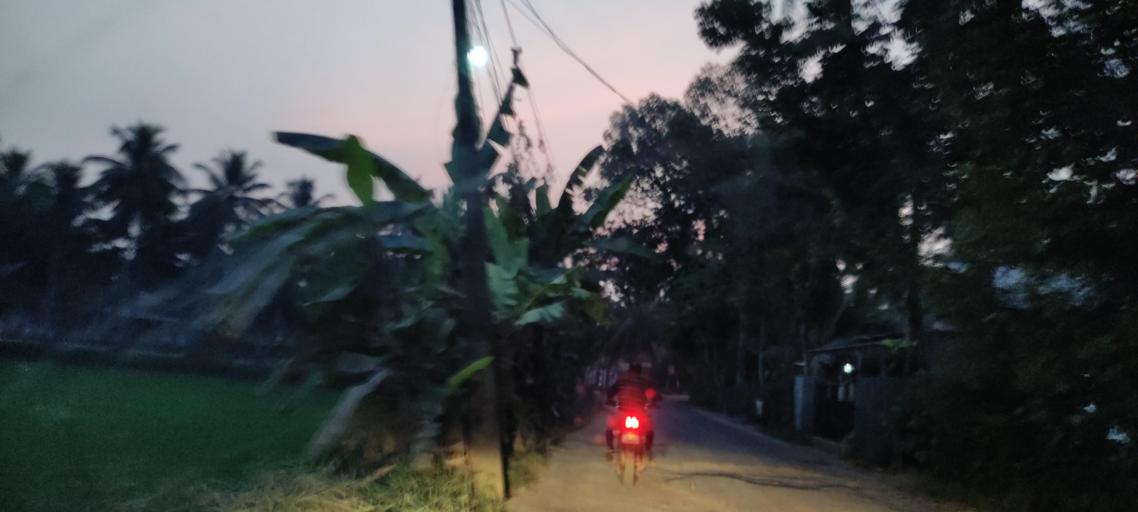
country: IN
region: Kerala
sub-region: Alappuzha
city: Mavelikara
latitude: 9.3212
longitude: 76.4540
